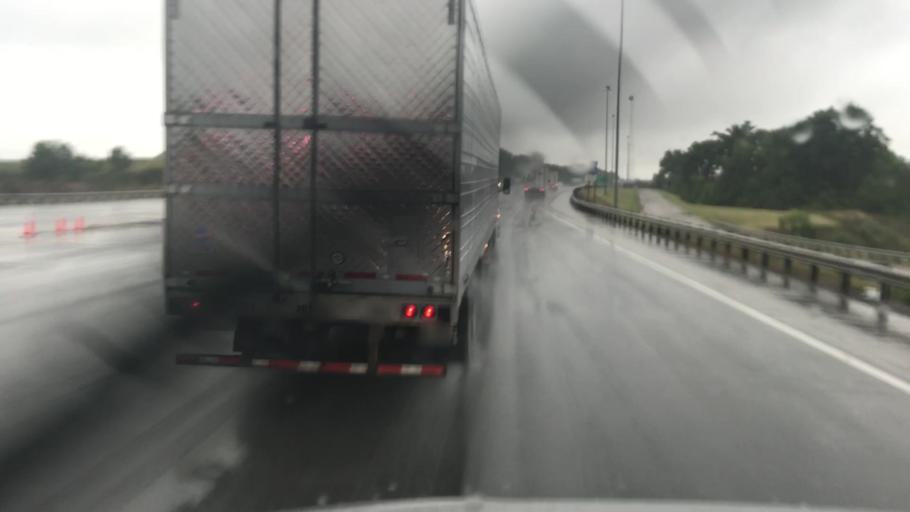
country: US
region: Ohio
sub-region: Mahoning County
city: New Middletown
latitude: 40.9252
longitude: -80.5583
